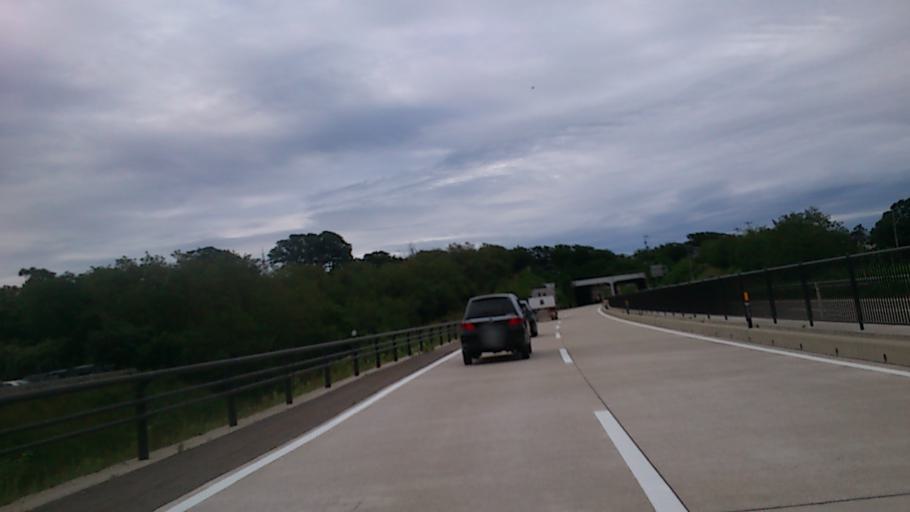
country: JP
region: Akita
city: Akita Shi
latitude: 39.6795
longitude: 140.0733
